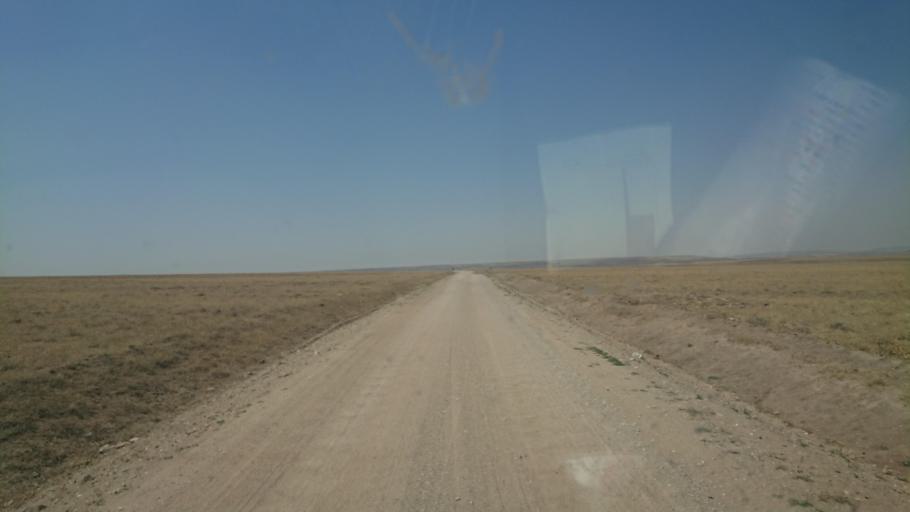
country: TR
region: Aksaray
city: Agacoren
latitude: 38.7438
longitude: 33.8911
